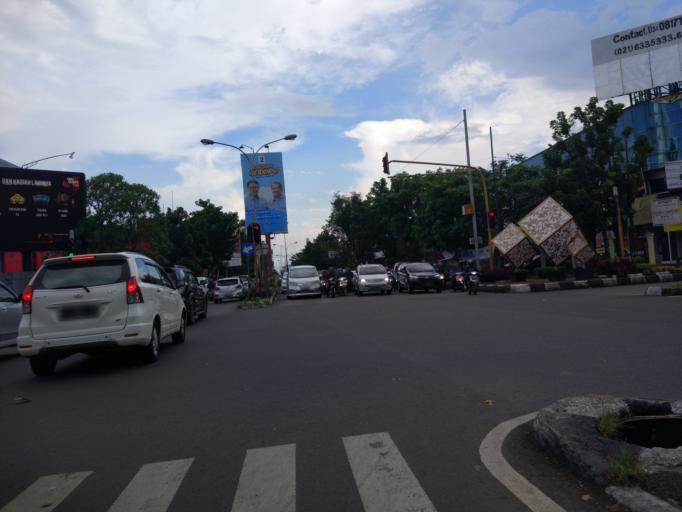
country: ID
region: West Java
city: Bandung
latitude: -6.9244
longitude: 107.6278
